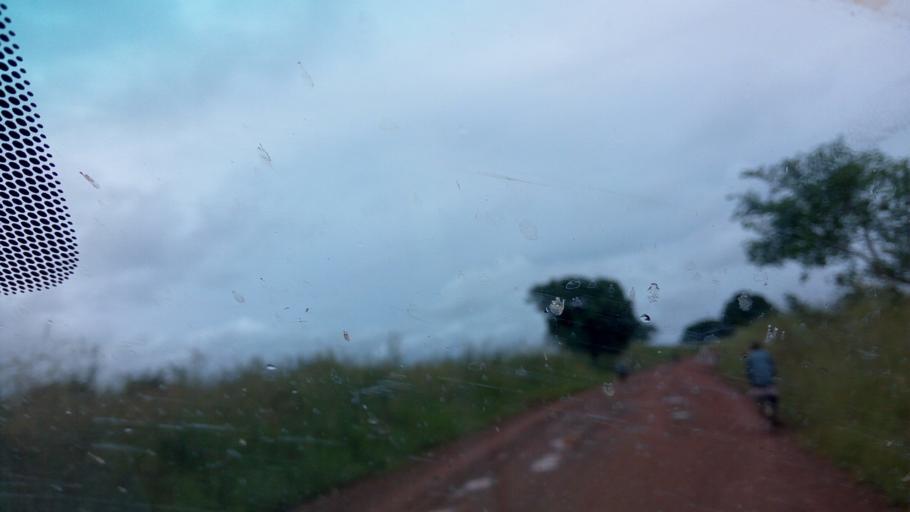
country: ZM
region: Luapula
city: Nchelenge
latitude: -9.1919
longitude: 28.2805
